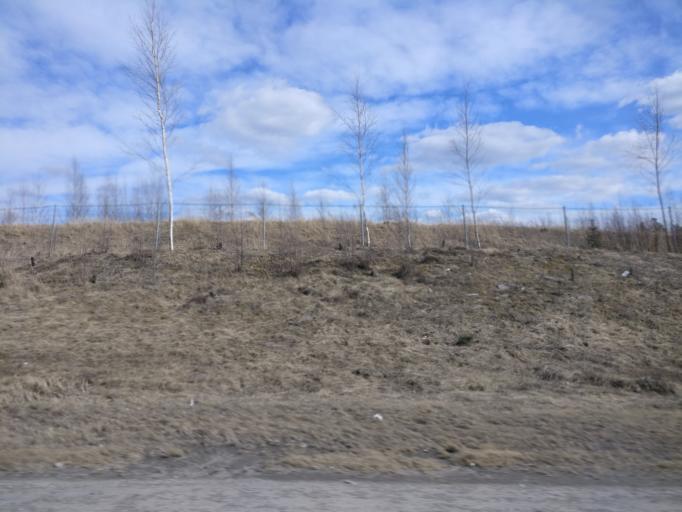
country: FI
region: Pirkanmaa
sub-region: Tampere
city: Lempaeaelae
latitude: 61.3495
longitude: 23.7898
